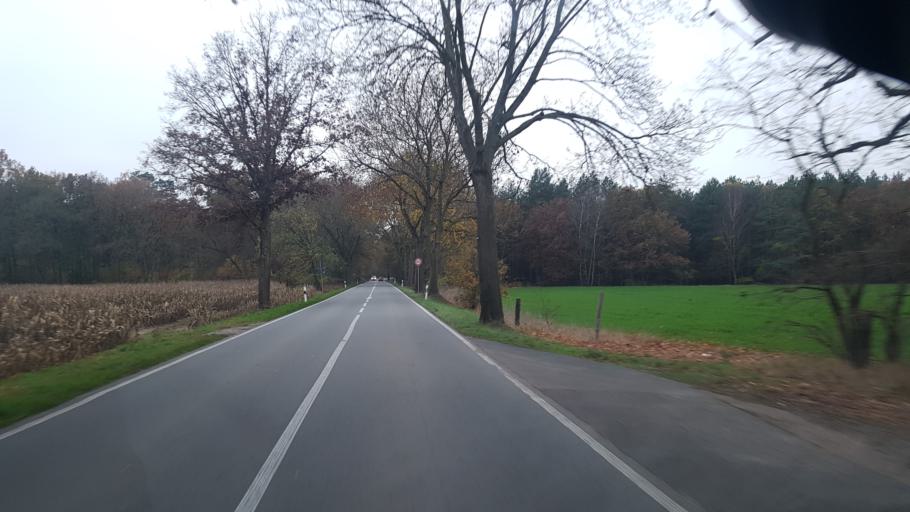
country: DE
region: Brandenburg
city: Ruthnick
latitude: 52.8969
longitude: 12.9454
